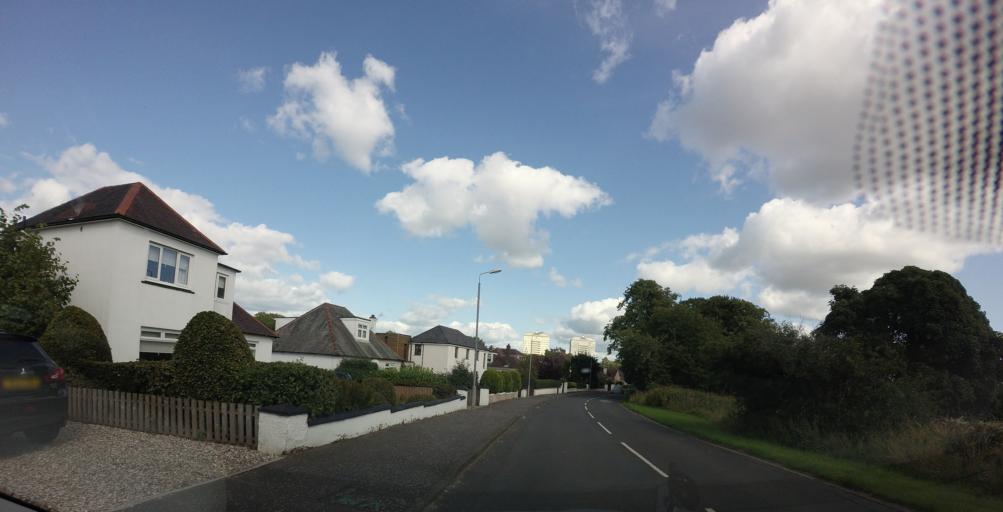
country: GB
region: Scotland
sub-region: North Lanarkshire
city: Coatbridge
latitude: 55.8602
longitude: -4.0494
